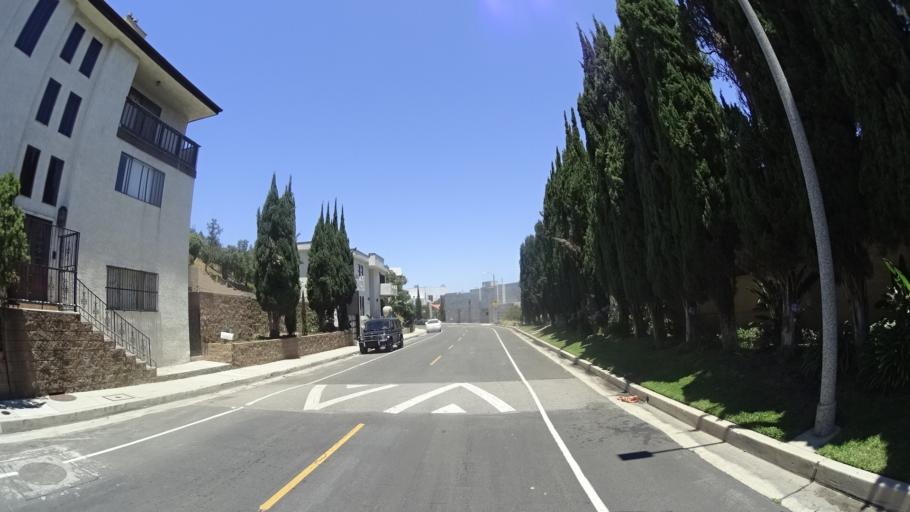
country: US
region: California
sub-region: Los Angeles County
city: West Hollywood
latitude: 34.1133
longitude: -118.3642
